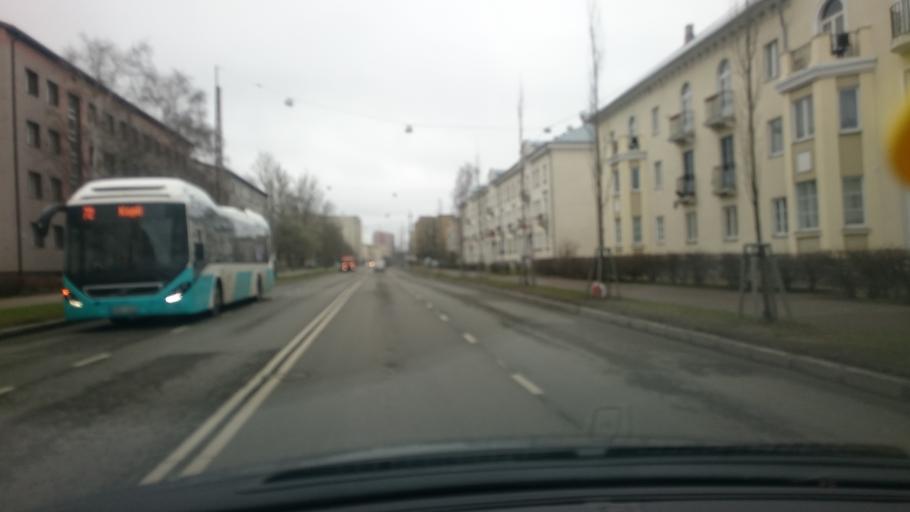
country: EE
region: Harju
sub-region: Tallinna linn
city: Tallinn
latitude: 59.4518
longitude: 24.6943
